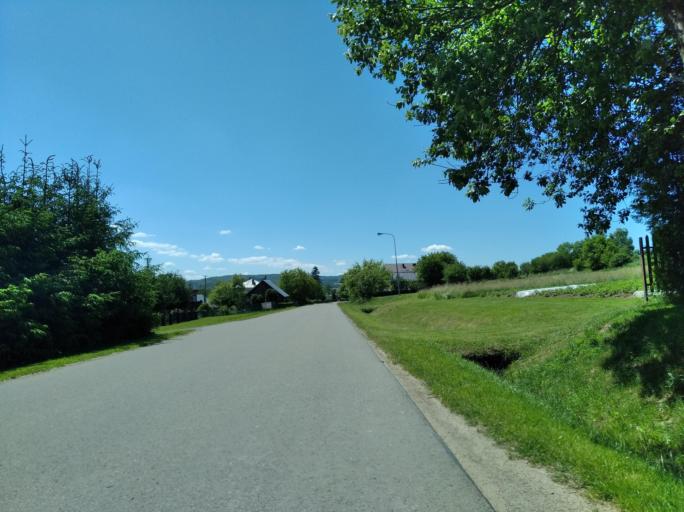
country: PL
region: Subcarpathian Voivodeship
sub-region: Powiat jasielski
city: Nowy Zmigrod
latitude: 49.6277
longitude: 21.5857
